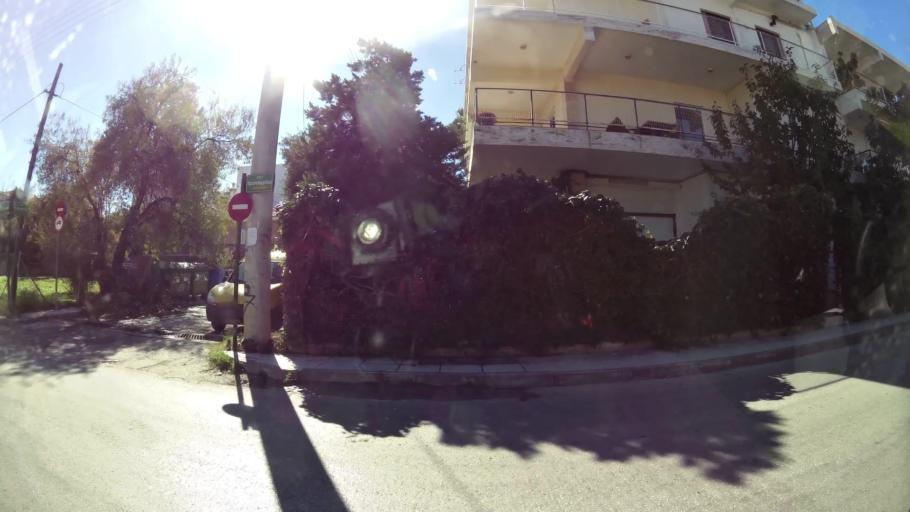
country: GR
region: Attica
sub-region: Nomarchia Anatolikis Attikis
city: Leondarion
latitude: 37.9879
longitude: 23.8604
